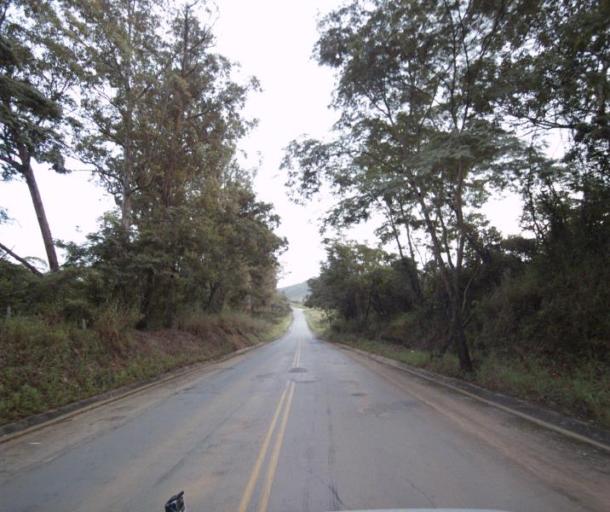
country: BR
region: Goias
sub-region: Pirenopolis
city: Pirenopolis
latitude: -15.8552
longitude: -48.7660
